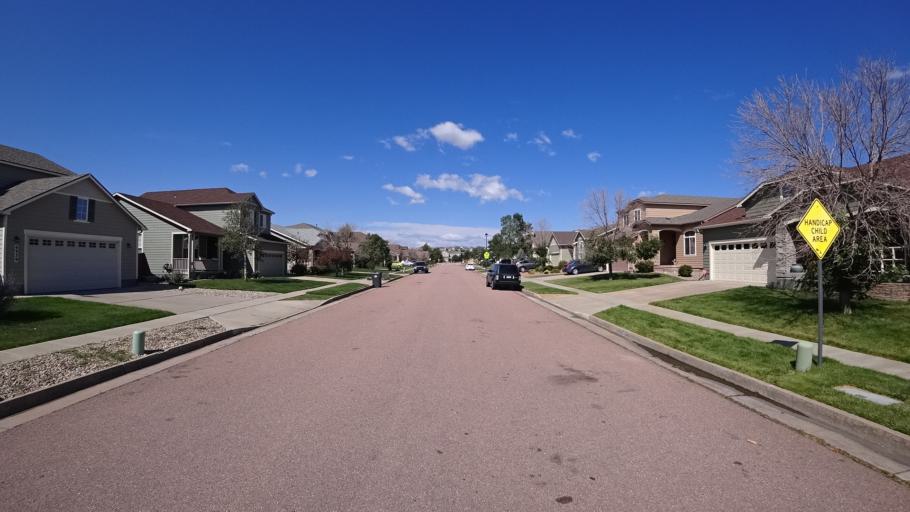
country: US
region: Colorado
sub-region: El Paso County
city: Cimarron Hills
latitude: 38.9223
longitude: -104.6981
